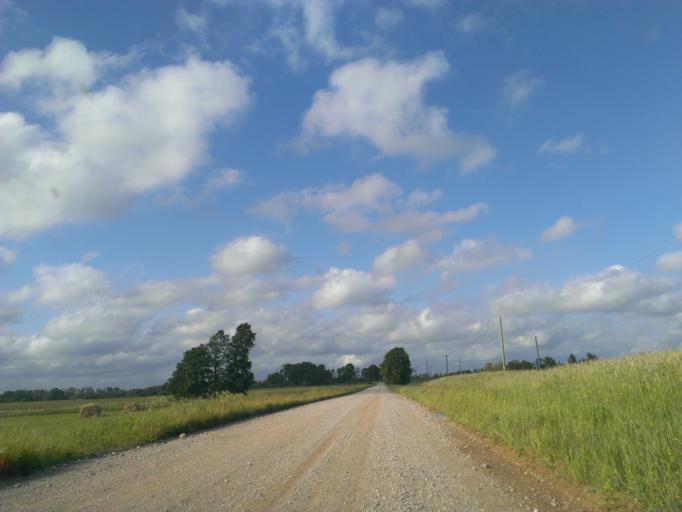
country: LV
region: Aizpute
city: Aizpute
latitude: 56.7564
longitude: 21.4561
